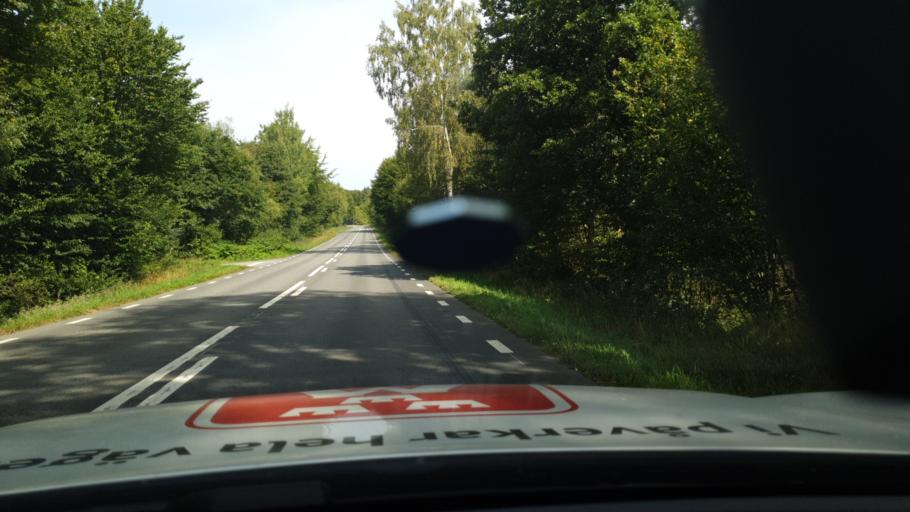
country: SE
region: Skane
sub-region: Simrishamns Kommun
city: Kivik
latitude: 55.6028
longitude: 14.1396
